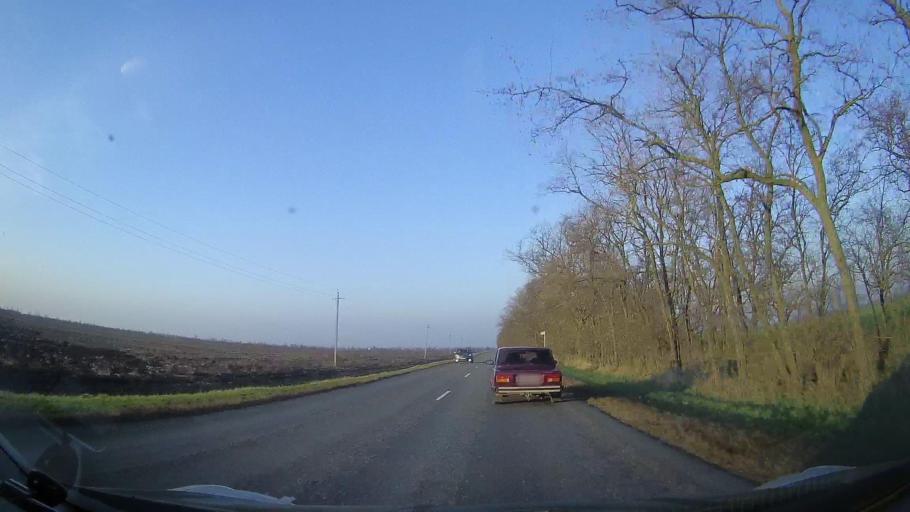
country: RU
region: Rostov
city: Ol'ginskaya
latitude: 47.0897
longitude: 39.9776
